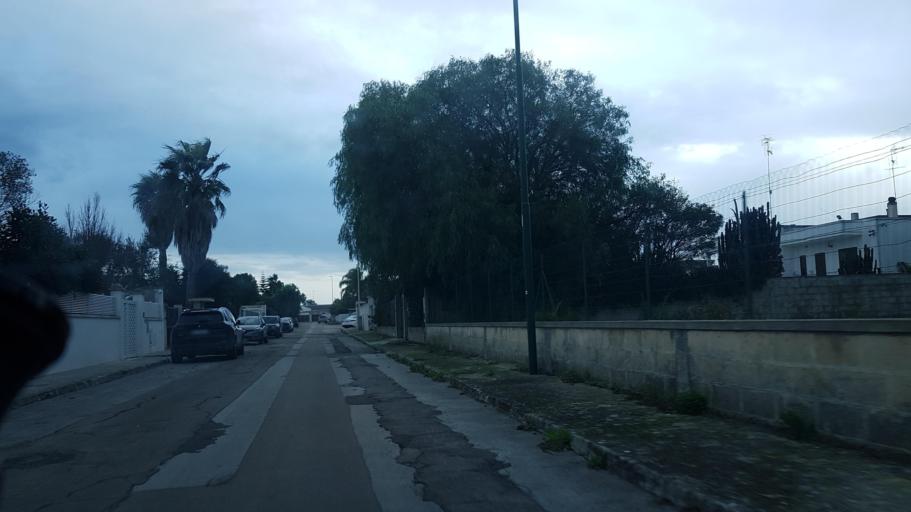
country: IT
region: Apulia
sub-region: Provincia di Lecce
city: Merine
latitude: 40.3396
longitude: 18.2172
